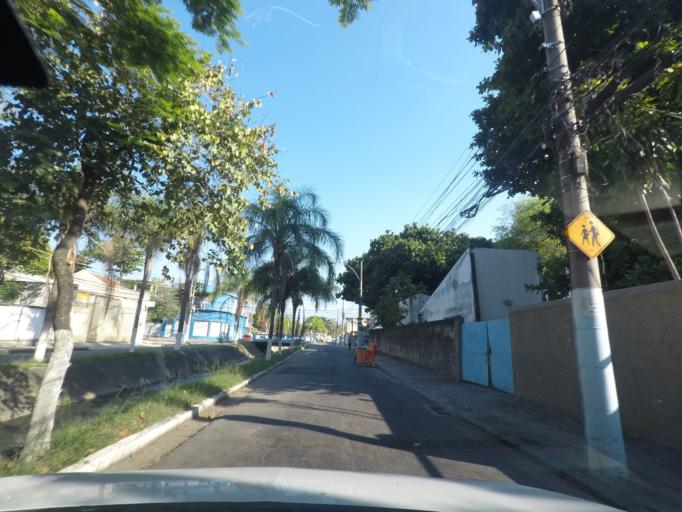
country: BR
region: Rio de Janeiro
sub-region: Duque De Caxias
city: Duque de Caxias
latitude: -22.8275
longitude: -43.2883
